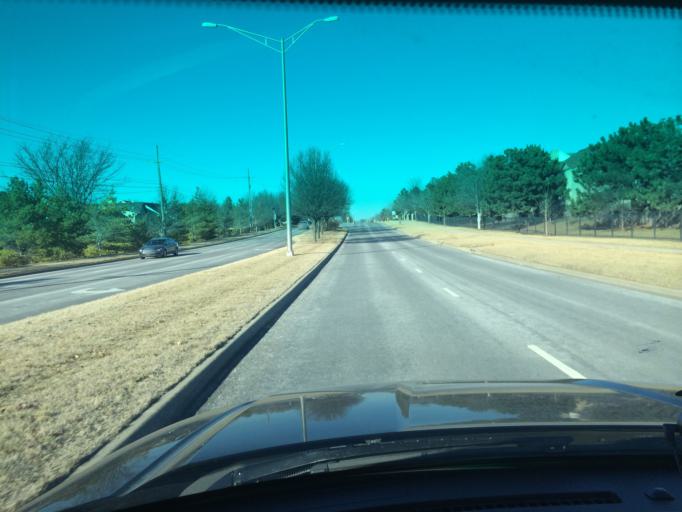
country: US
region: Kansas
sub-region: Johnson County
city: Lenexa
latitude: 38.8877
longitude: -94.7423
